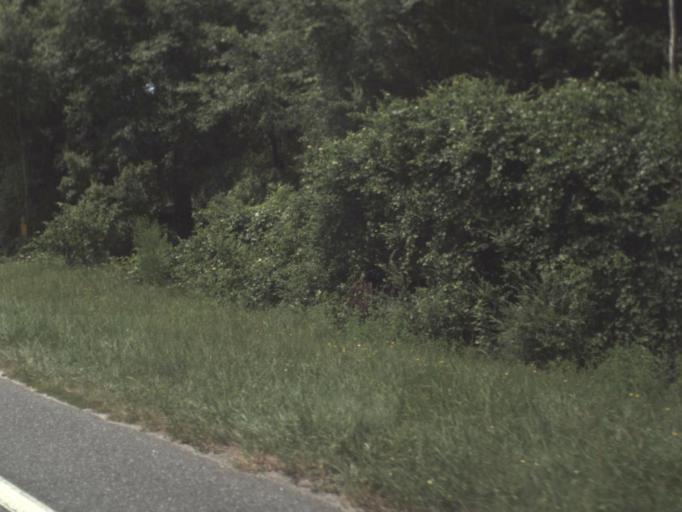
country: US
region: Florida
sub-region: Hamilton County
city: Jasper
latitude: 30.5703
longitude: -83.0783
